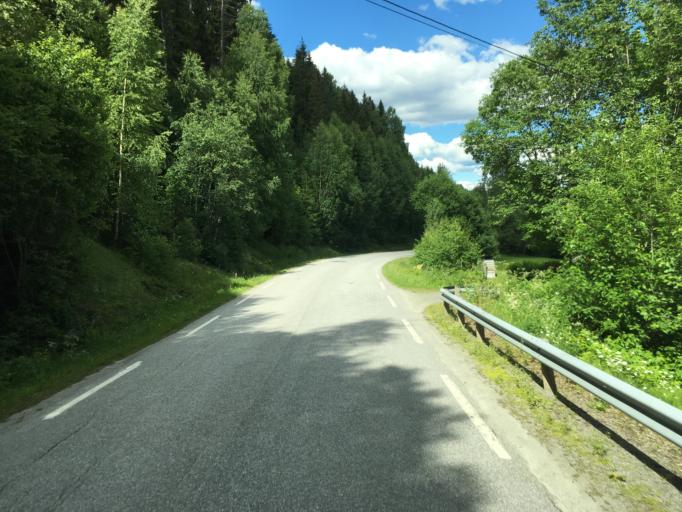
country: NO
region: Oppland
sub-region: Sondre Land
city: Hov
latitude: 60.5766
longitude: 10.2909
